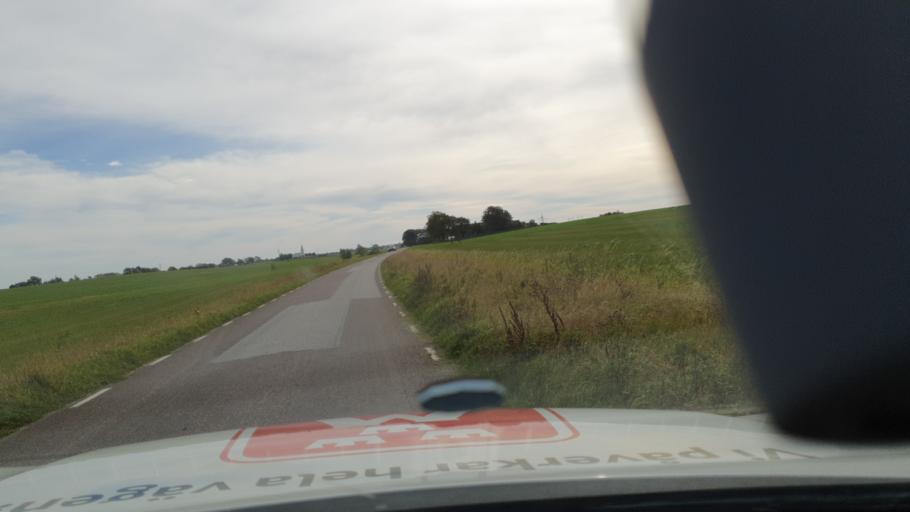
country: SE
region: Skane
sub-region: Vellinge Kommun
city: Vellinge
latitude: 55.4970
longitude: 13.0331
